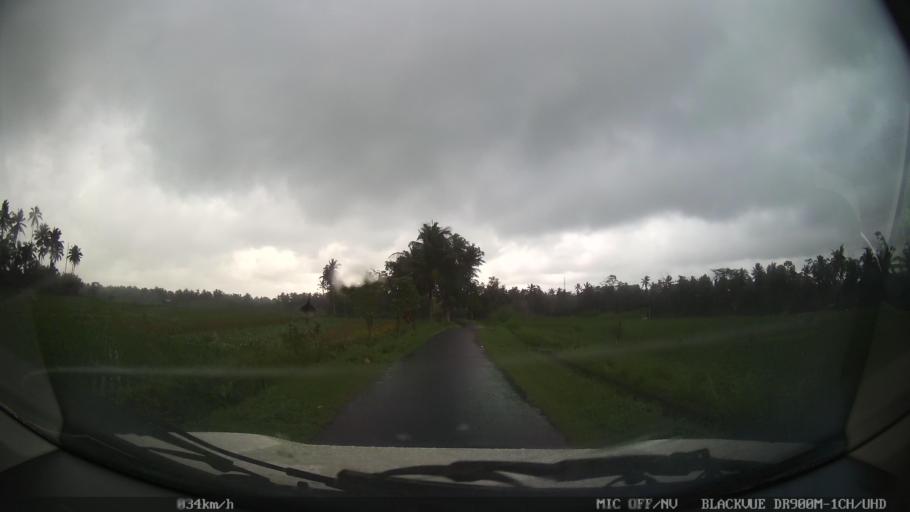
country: ID
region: Bali
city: Kekeran
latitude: -8.4847
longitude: 115.1872
